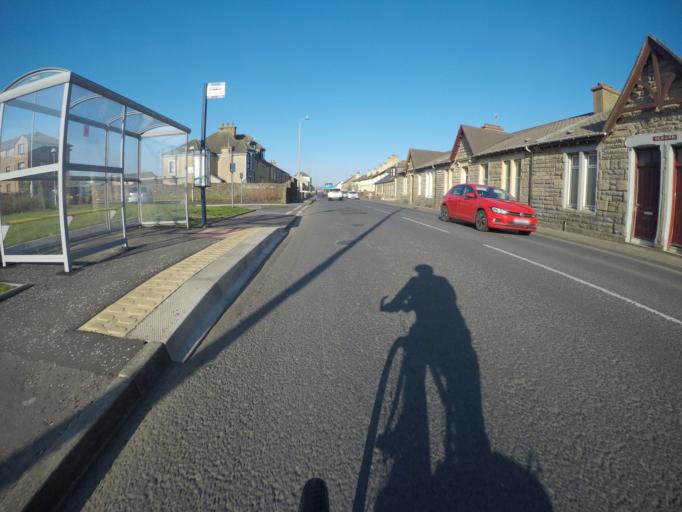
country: GB
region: Scotland
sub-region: North Ayrshire
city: Saltcoats
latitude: 55.6340
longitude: -4.7795
